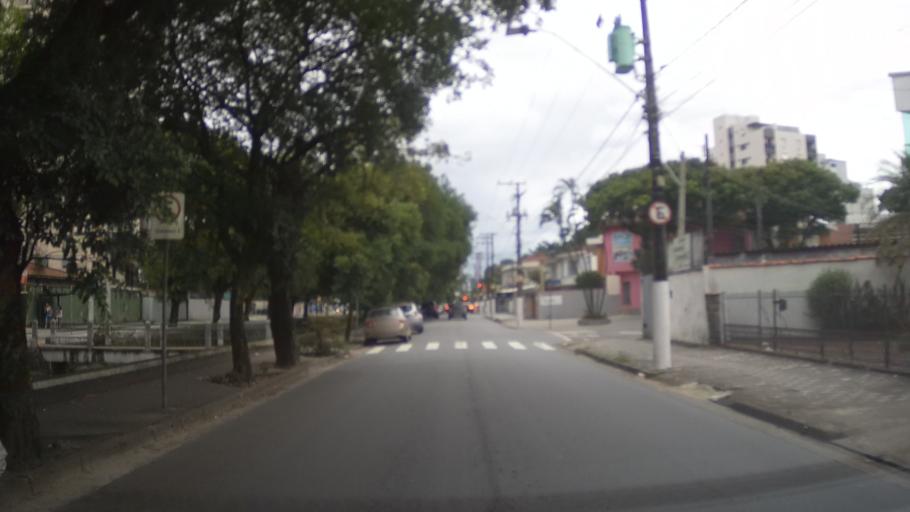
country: BR
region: Sao Paulo
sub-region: Santos
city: Santos
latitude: -23.9699
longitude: -46.3075
